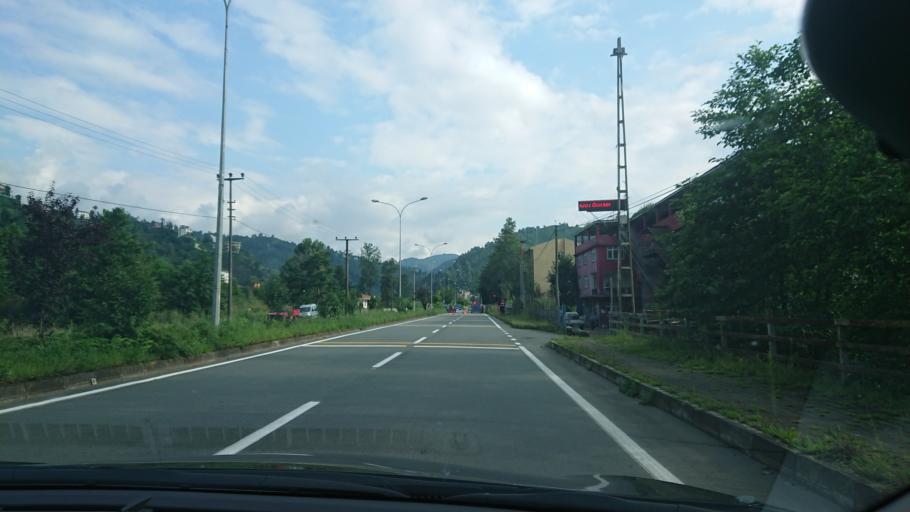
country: TR
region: Rize
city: Rize
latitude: 40.9742
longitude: 40.5332
